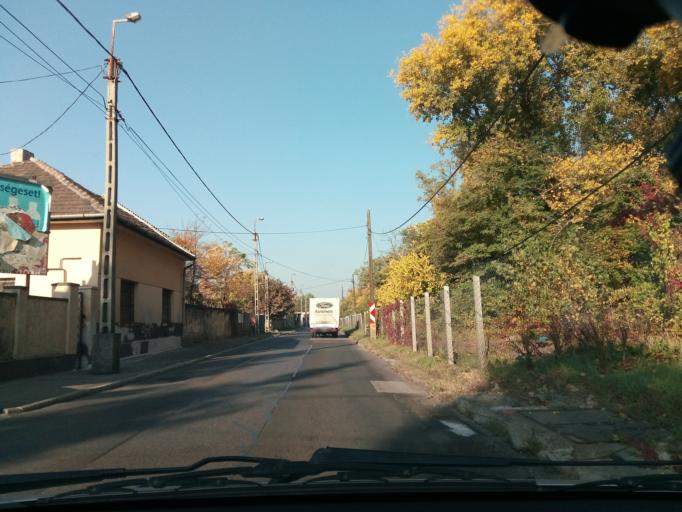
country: HU
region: Budapest
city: Budapest XIX. keruelet
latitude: 47.4637
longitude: 19.1350
